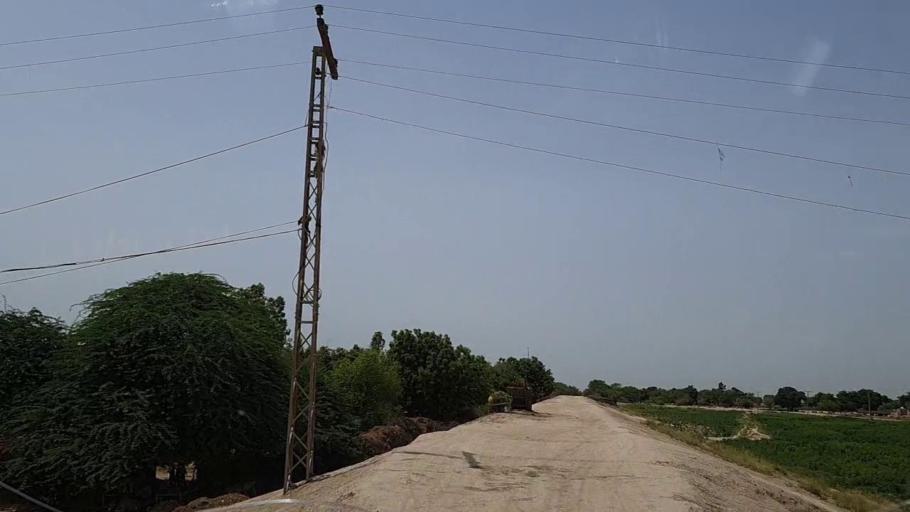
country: PK
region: Sindh
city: Tharu Shah
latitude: 27.0309
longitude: 68.1137
